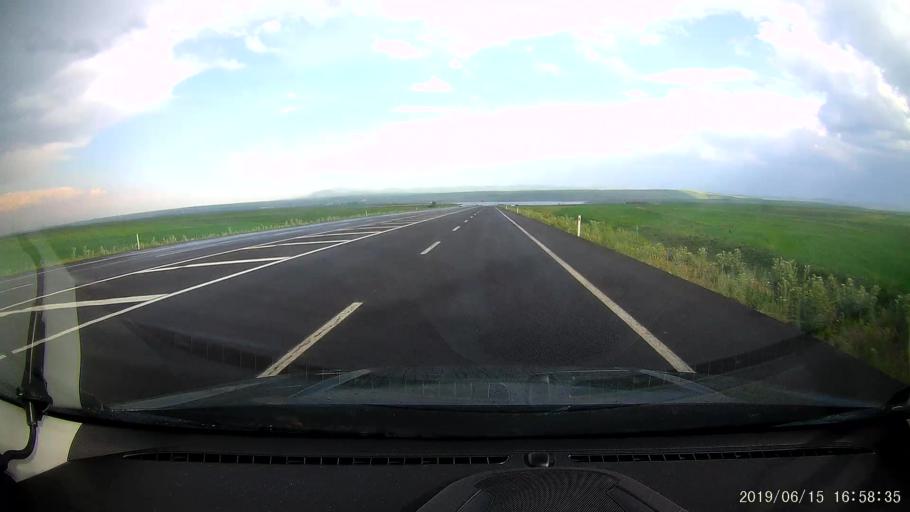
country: TR
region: Kars
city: Susuz
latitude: 40.7633
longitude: 43.1443
